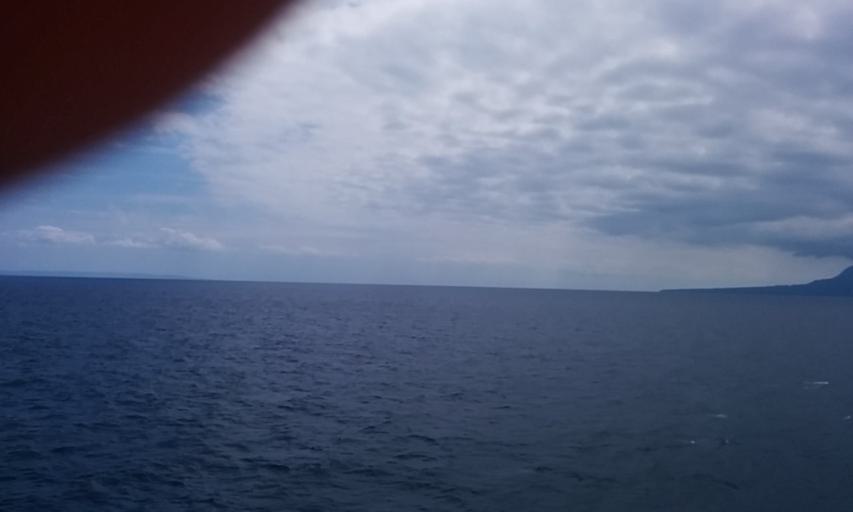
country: JP
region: Kagoshima
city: Nishinoomote
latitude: 30.5153
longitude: 130.6118
